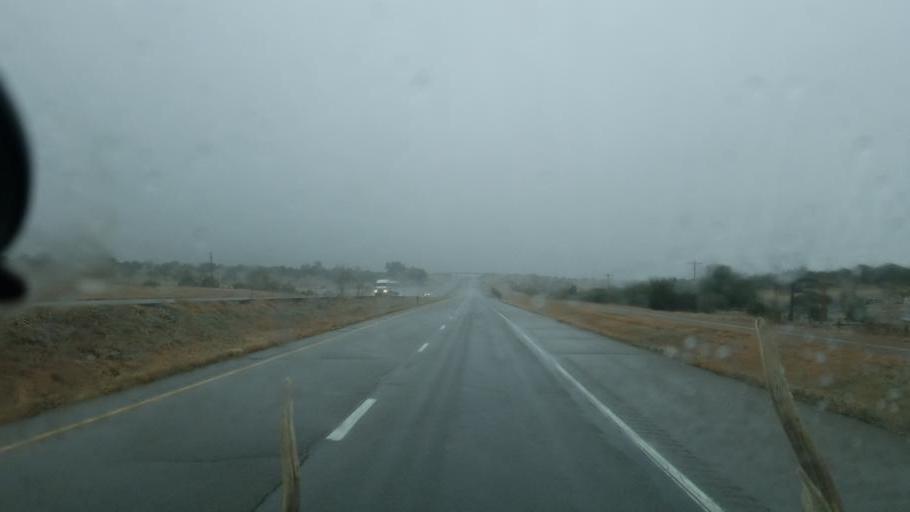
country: US
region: Colorado
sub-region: Pueblo County
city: Colorado City
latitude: 38.0637
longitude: -104.7142
